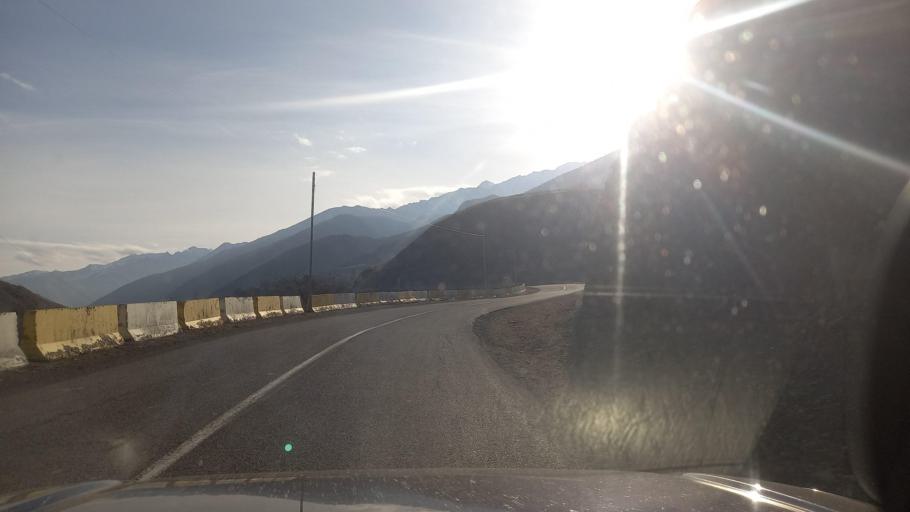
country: RU
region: Ingushetiya
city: Dzhayrakh
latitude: 42.8311
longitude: 44.6669
